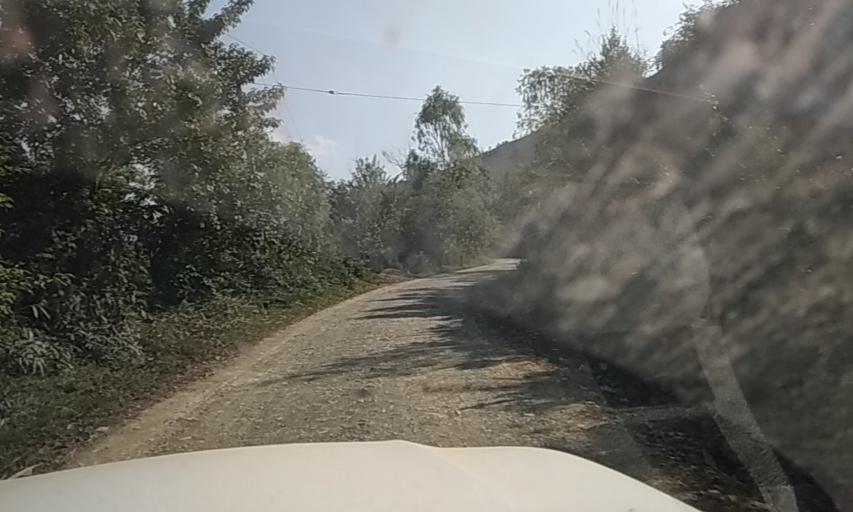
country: LA
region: Phongsali
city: Phongsali
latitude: 21.6558
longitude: 102.0909
